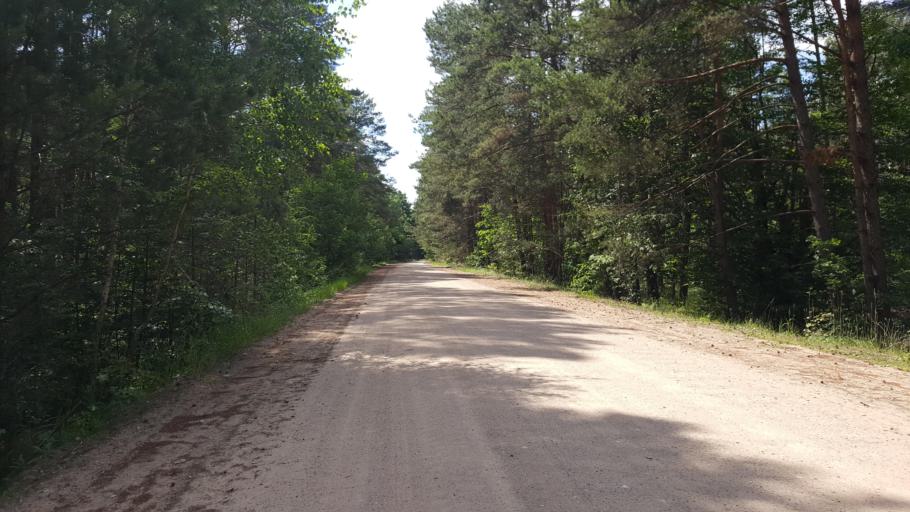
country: BY
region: Brest
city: Kamyanyuki
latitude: 52.5538
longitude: 23.6778
